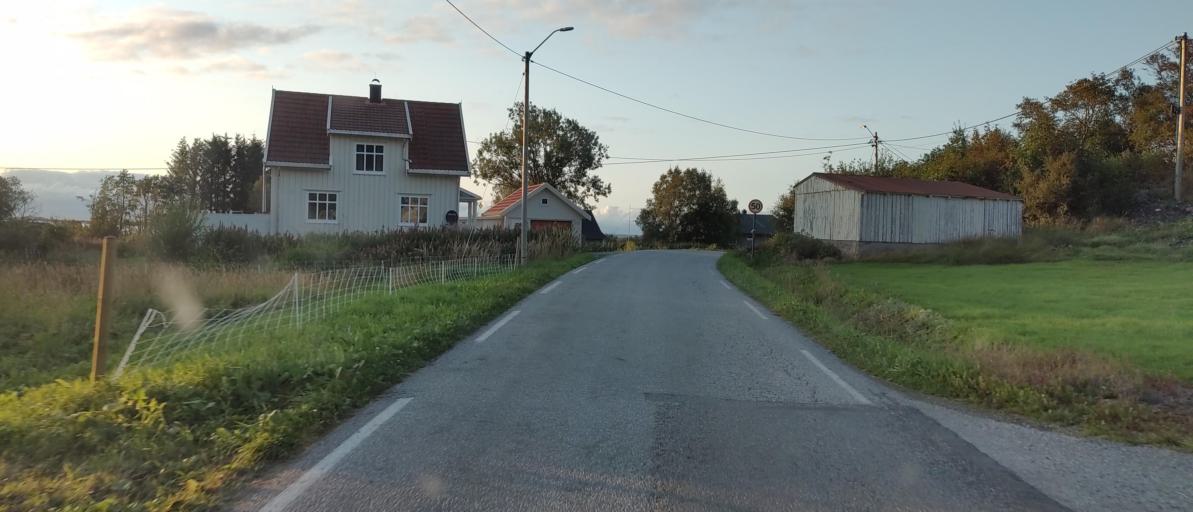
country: NO
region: More og Romsdal
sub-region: Fraena
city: Elnesvagen
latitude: 62.9940
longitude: 7.2202
